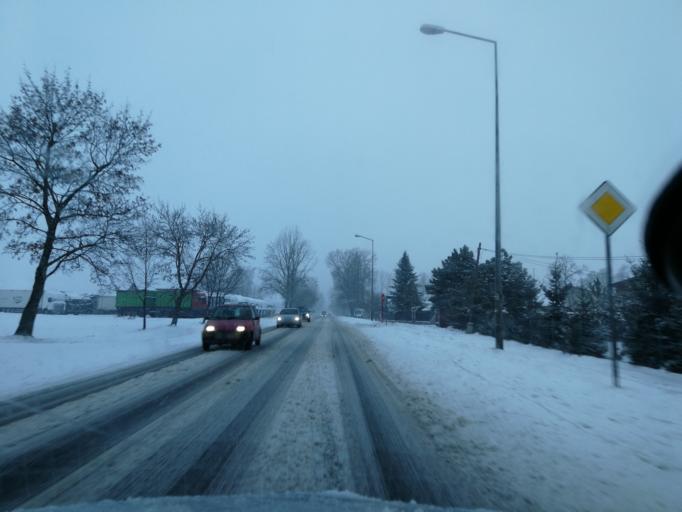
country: PL
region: Silesian Voivodeship
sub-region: Powiat pszczynski
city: Czarkow
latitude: 49.9893
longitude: 18.9167
